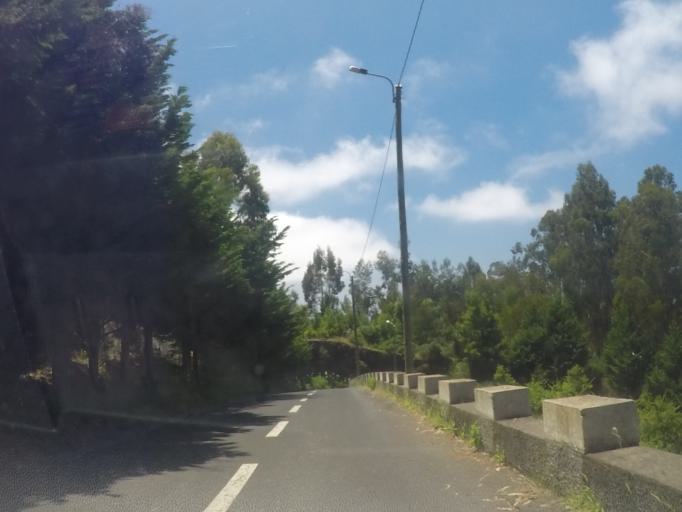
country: PT
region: Madeira
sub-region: Camara de Lobos
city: Curral das Freiras
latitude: 32.6903
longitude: -16.9743
